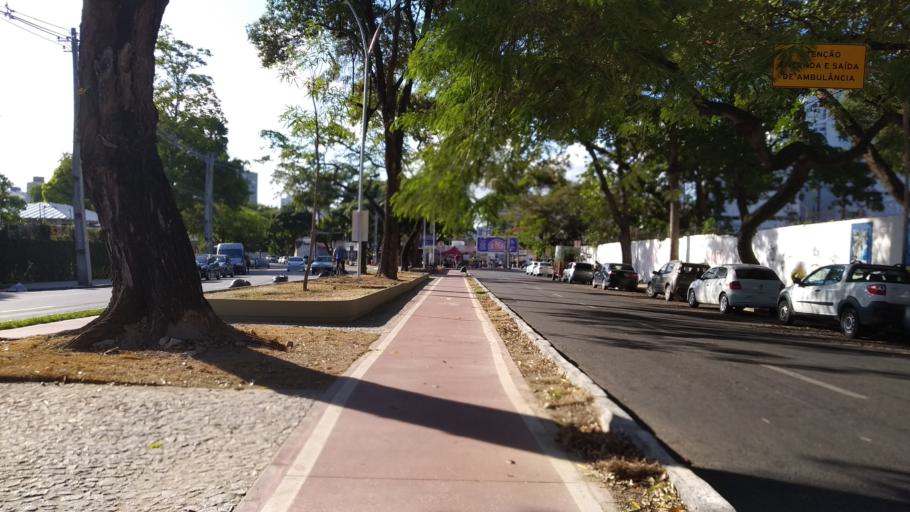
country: BR
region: Pernambuco
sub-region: Recife
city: Recife
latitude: -8.0505
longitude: -34.8866
